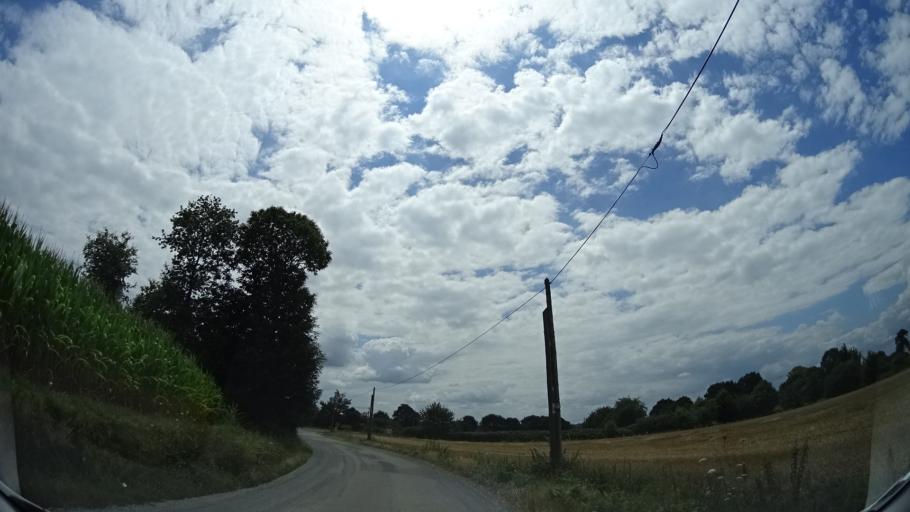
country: FR
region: Brittany
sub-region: Departement d'Ille-et-Vilaine
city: Pace
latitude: 48.1779
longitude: -1.7664
